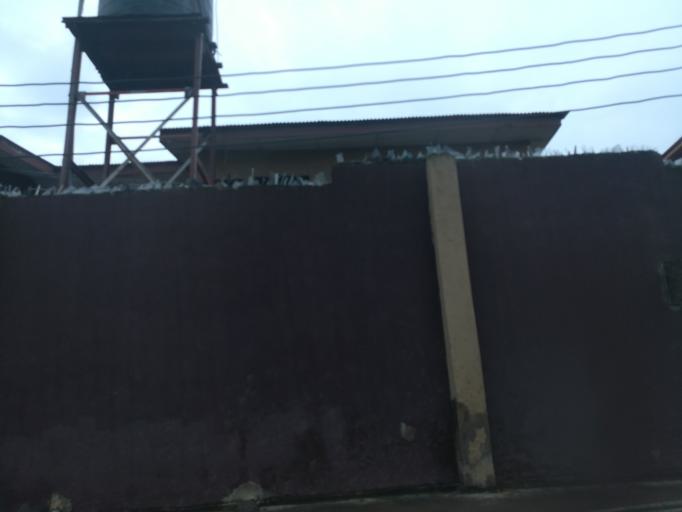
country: NG
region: Lagos
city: Makoko
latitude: 6.4919
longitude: 3.3849
